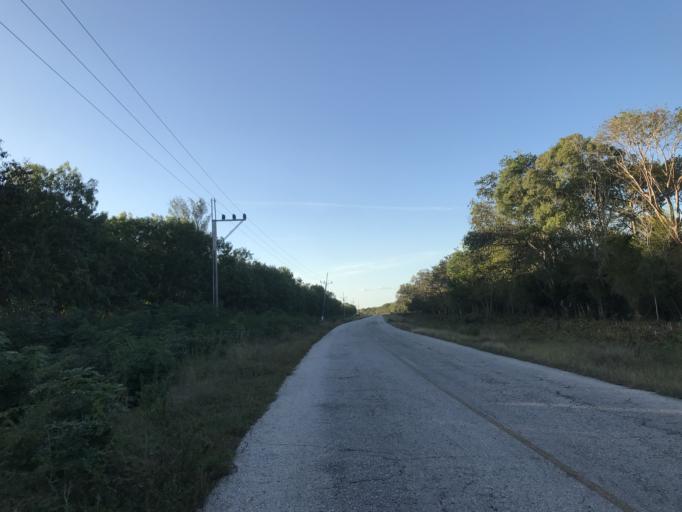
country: CU
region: Cienfuegos
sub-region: Municipio de Aguada de Pasajeros
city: Aguada de Pasajeros
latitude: 22.0700
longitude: -81.0532
